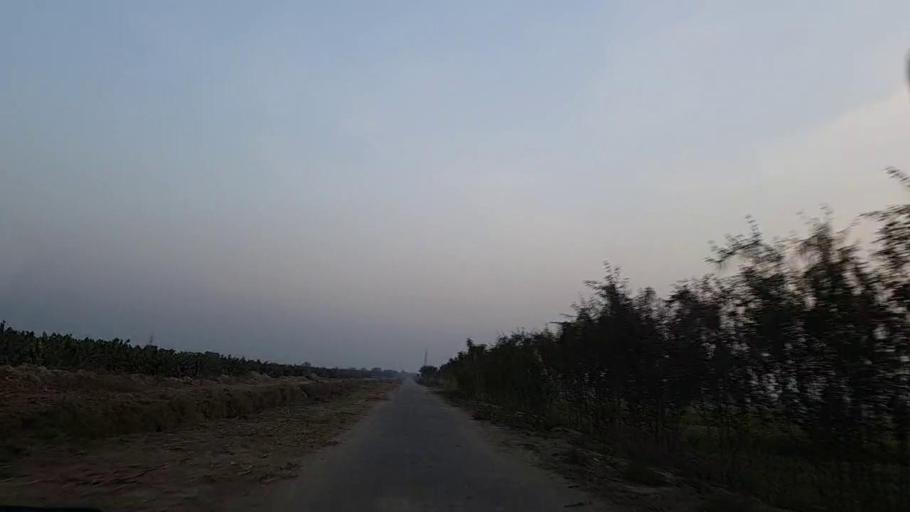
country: PK
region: Sindh
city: Tando Ghulam Ali
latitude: 25.1146
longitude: 68.8989
